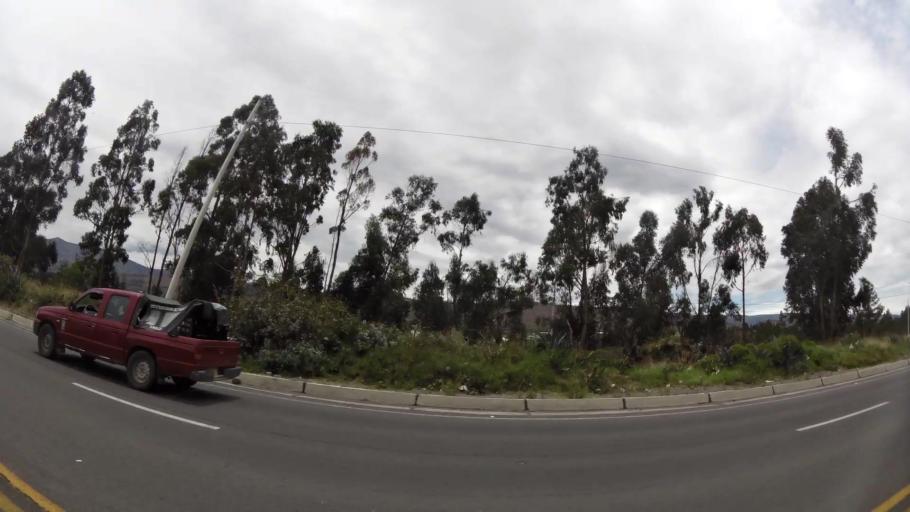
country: EC
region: Cotopaxi
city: San Miguel de Salcedo
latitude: -1.0132
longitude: -78.5926
